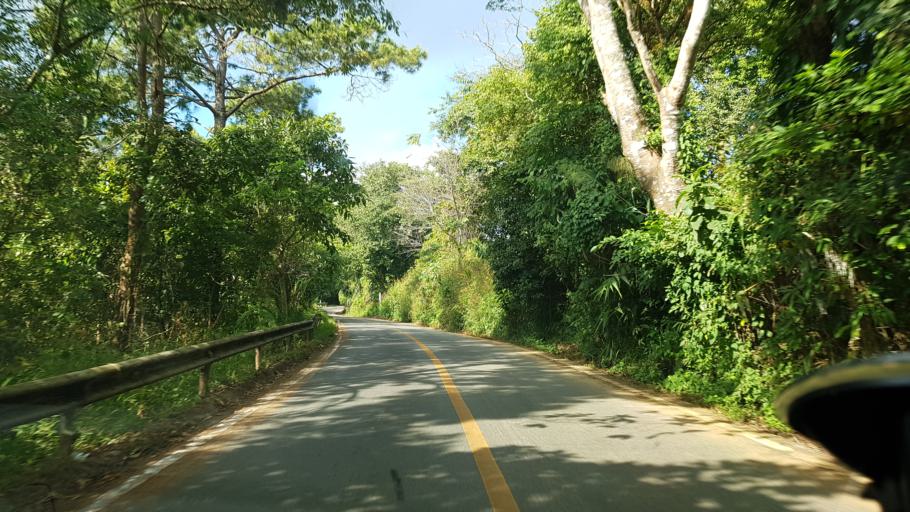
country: TH
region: Chiang Rai
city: Mae Fa Luang
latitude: 20.3265
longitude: 99.8158
